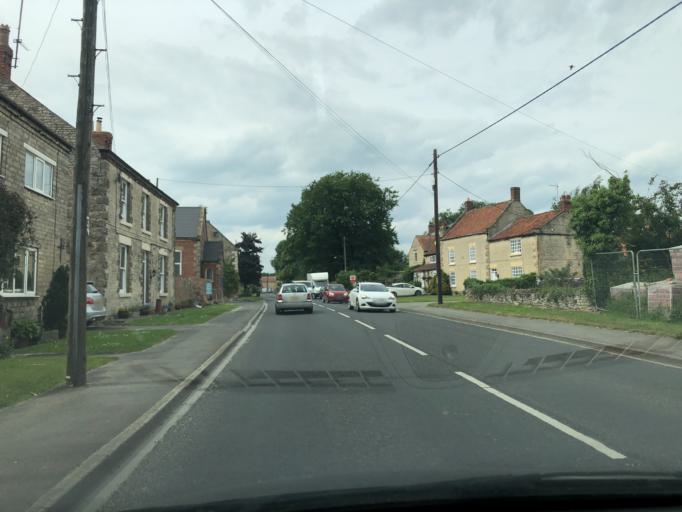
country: GB
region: England
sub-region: North Yorkshire
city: Pickering
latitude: 54.2570
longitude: -0.7992
